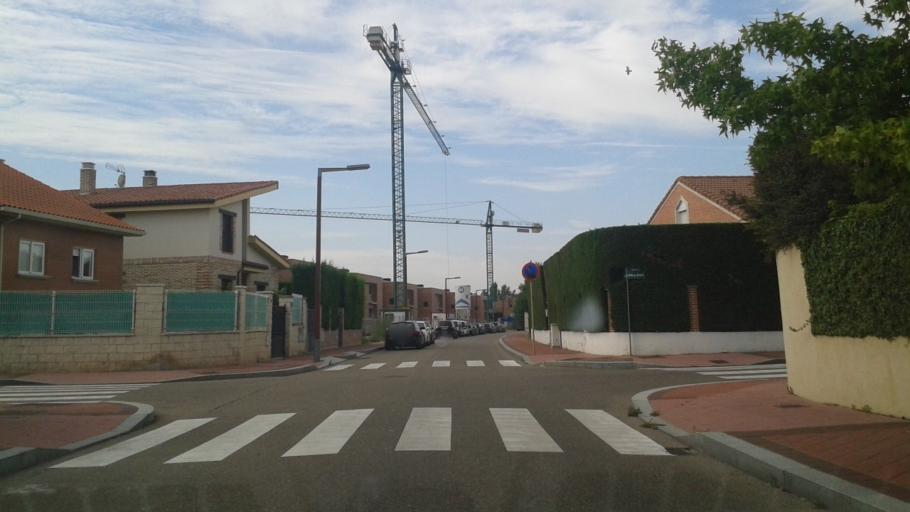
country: ES
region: Castille and Leon
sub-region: Provincia de Valladolid
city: Arroyo
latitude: 41.6145
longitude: -4.7787
